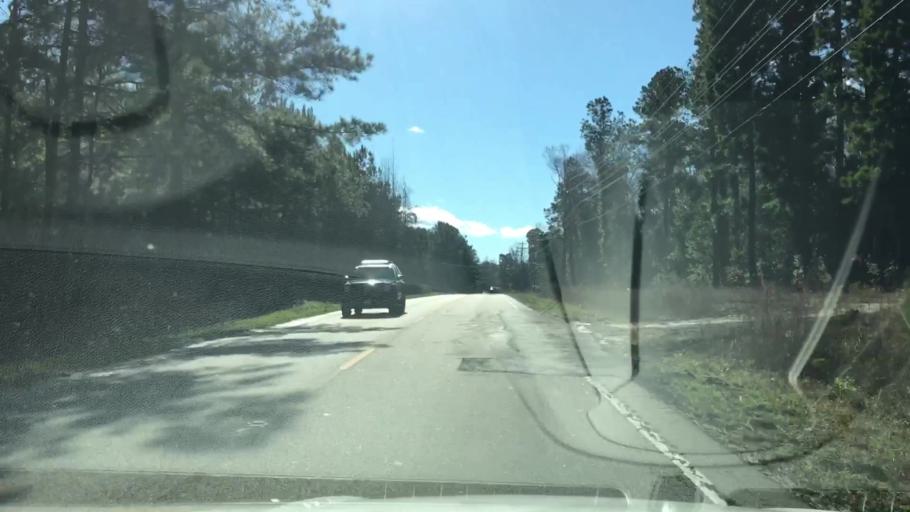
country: US
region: South Carolina
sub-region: Dorchester County
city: Summerville
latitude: 33.0714
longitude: -80.2204
